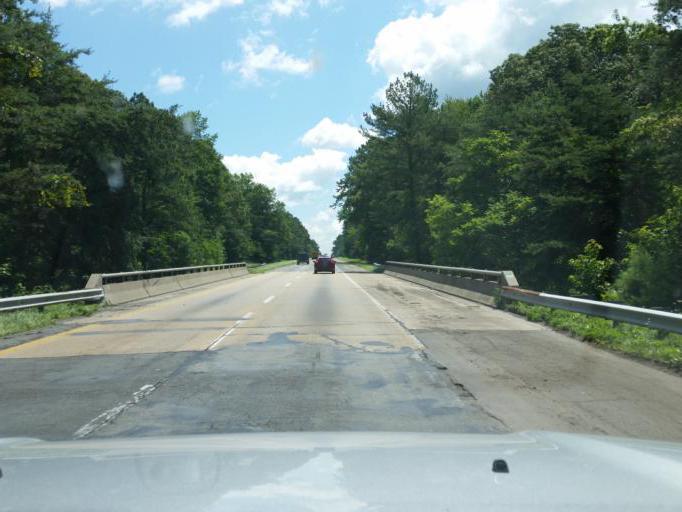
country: US
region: Virginia
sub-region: New Kent County
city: New Kent
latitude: 37.4951
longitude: -77.0243
